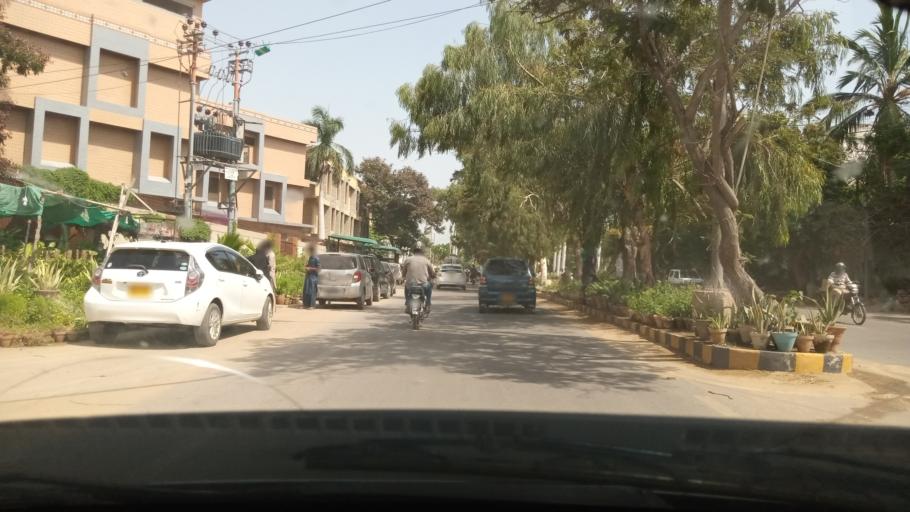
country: PK
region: Sindh
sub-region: Karachi District
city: Karachi
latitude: 24.8785
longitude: 67.0430
